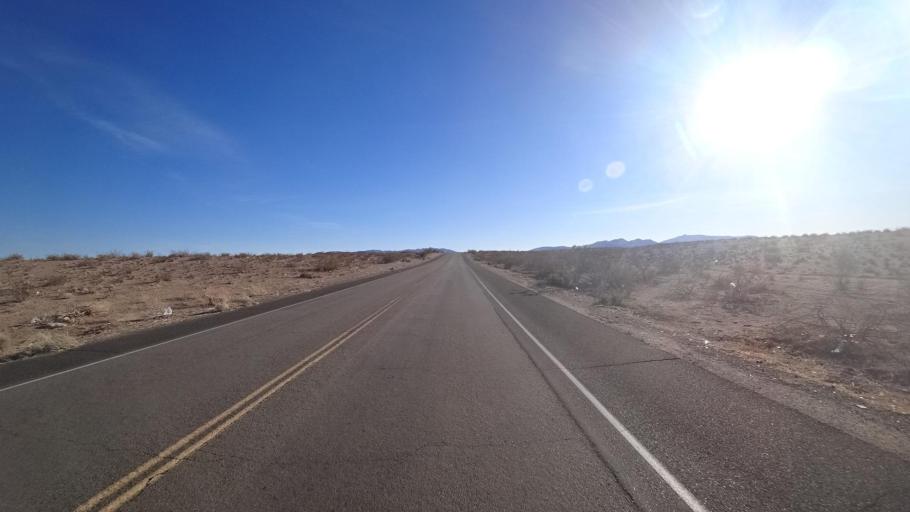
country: US
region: California
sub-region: Kern County
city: China Lake Acres
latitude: 35.6185
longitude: -117.7230
